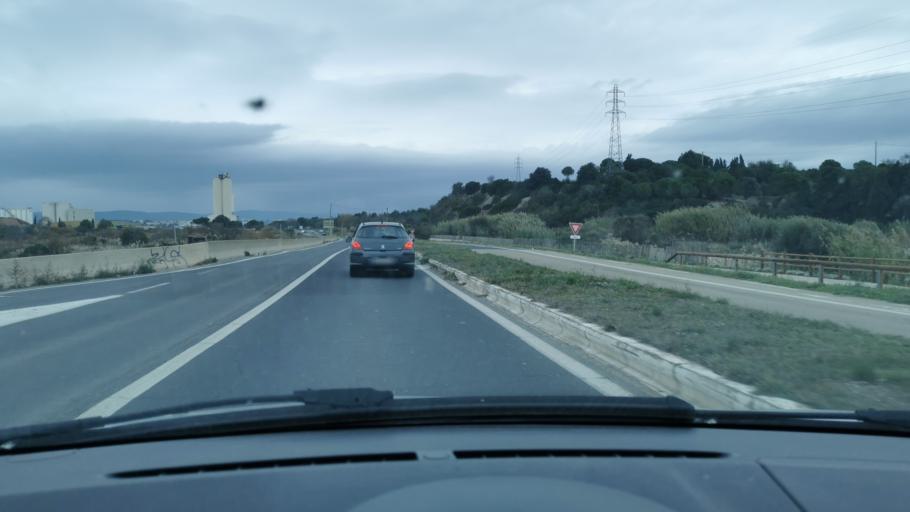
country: FR
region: Languedoc-Roussillon
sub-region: Departement de l'Herault
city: Sete
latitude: 43.4242
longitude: 3.7082
